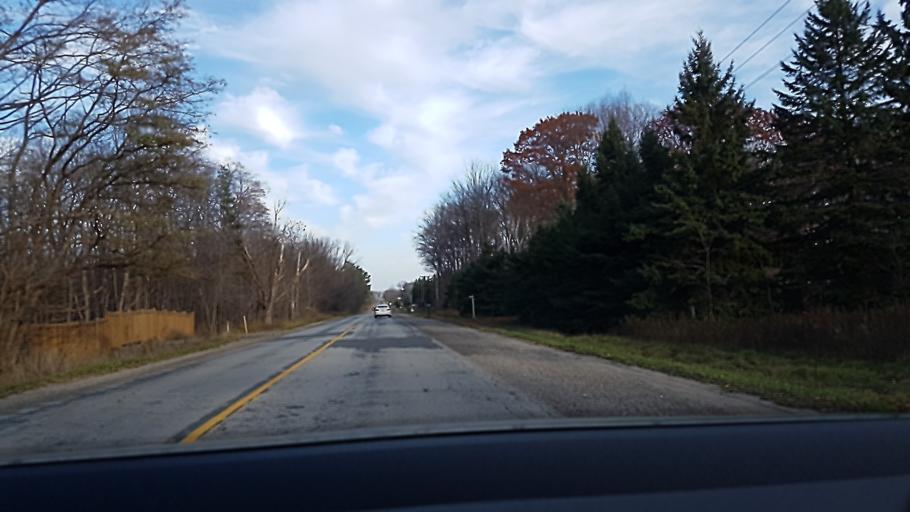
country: CA
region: Ontario
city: Barrie
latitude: 44.3684
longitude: -79.5972
